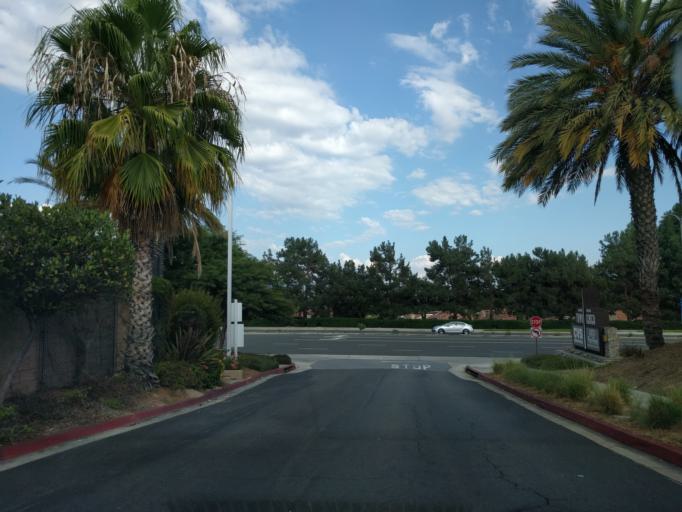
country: US
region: California
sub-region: Orange County
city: Aliso Viejo
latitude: 33.5717
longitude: -117.7240
